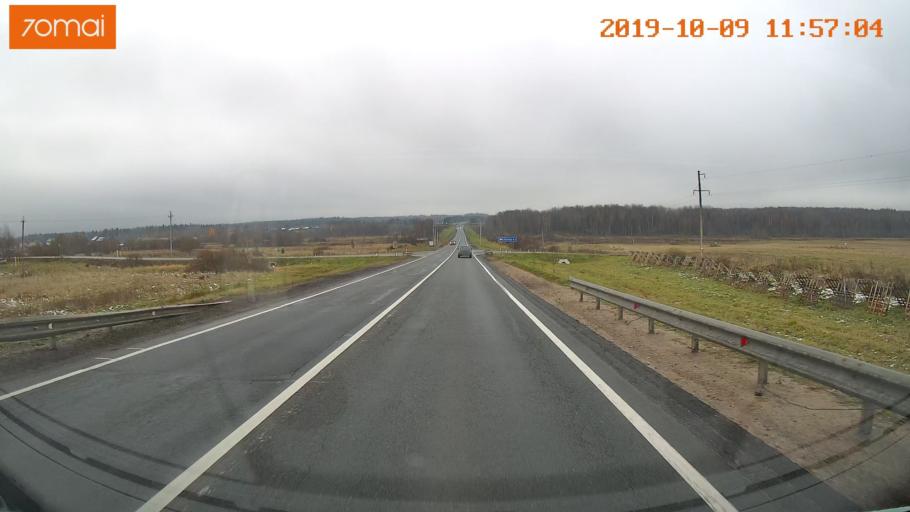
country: RU
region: Vologda
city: Gryazovets
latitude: 58.7369
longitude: 40.2906
